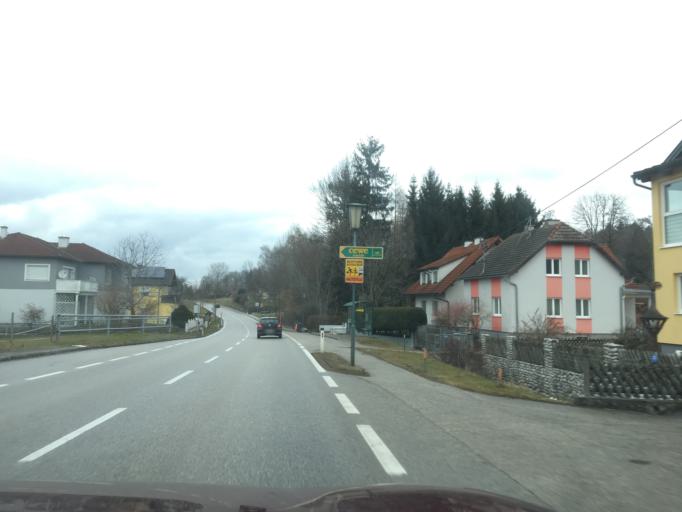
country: AT
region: Upper Austria
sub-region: Politischer Bezirk Kirchdorf an der Krems
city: Kremsmunster
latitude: 47.9658
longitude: 14.1307
